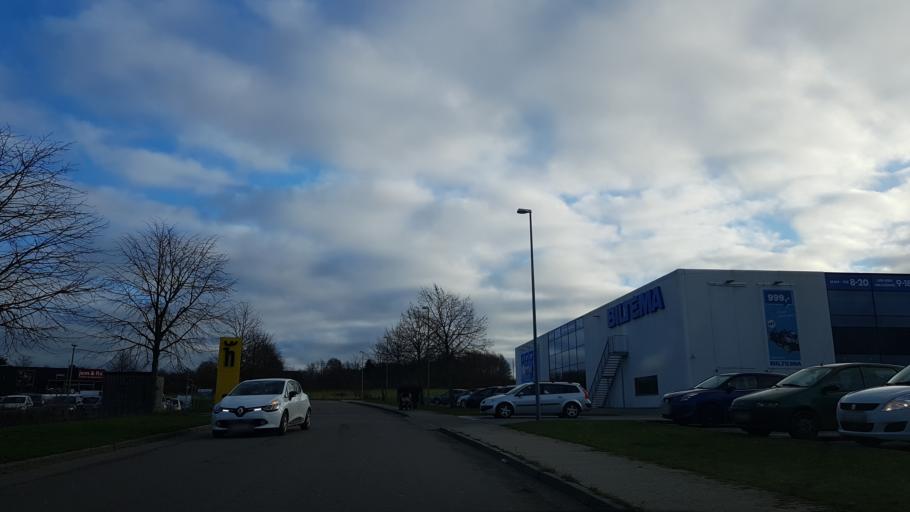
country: DK
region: Zealand
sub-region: Slagelse Kommune
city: Slagelse
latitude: 55.3867
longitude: 11.3276
